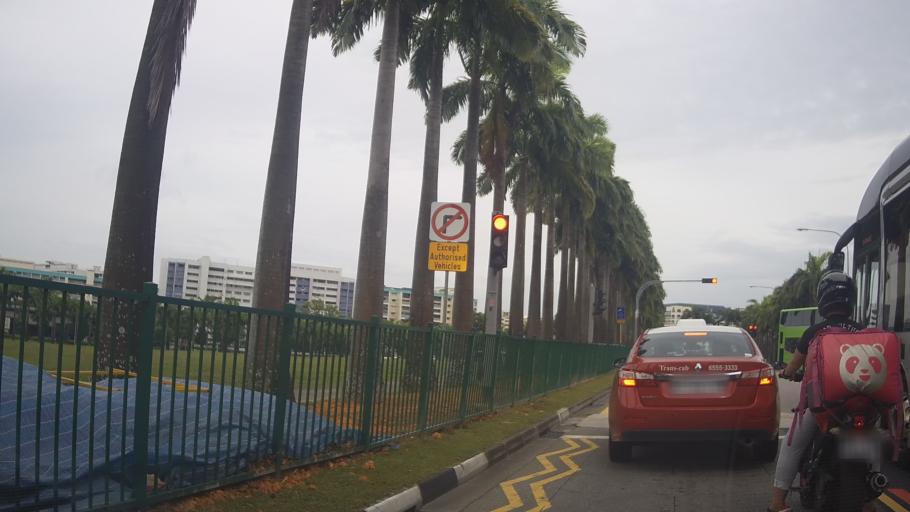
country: MY
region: Johor
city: Johor Bahru
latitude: 1.4382
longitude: 103.7853
